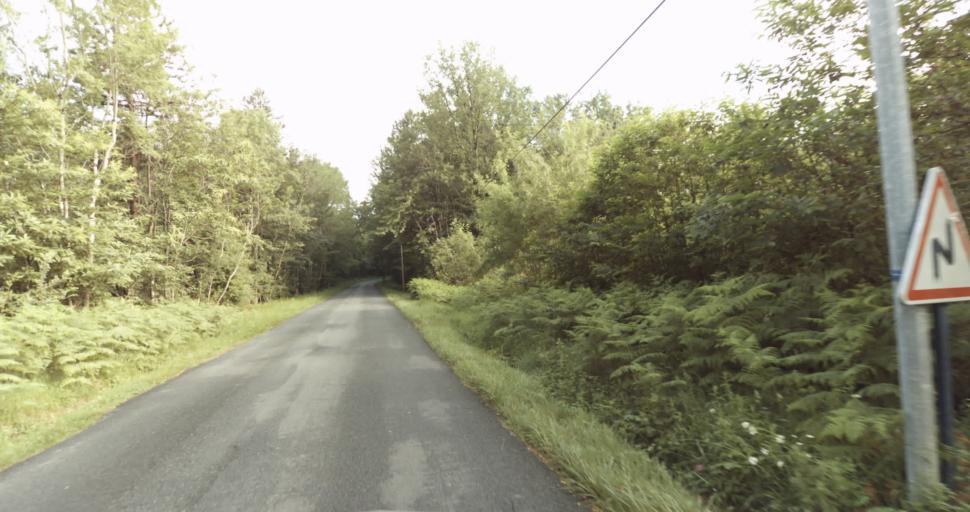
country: FR
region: Aquitaine
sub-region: Departement de la Dordogne
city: Le Bugue
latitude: 44.9305
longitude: 0.8189
